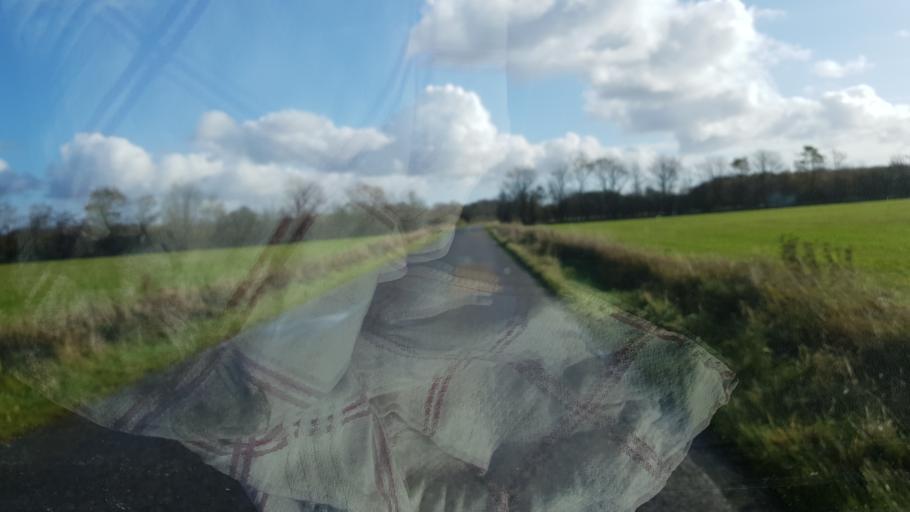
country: DK
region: South Denmark
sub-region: Varde Kommune
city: Olgod
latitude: 55.6916
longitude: 8.6532
